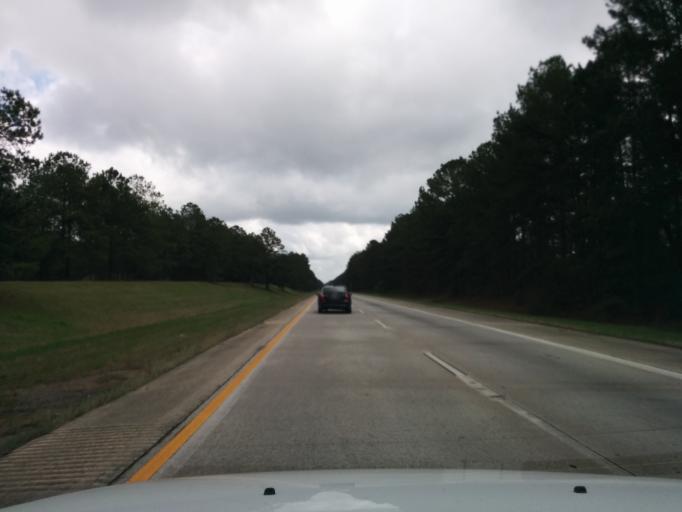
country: US
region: Georgia
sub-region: Evans County
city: Claxton
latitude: 32.2984
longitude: -81.8306
